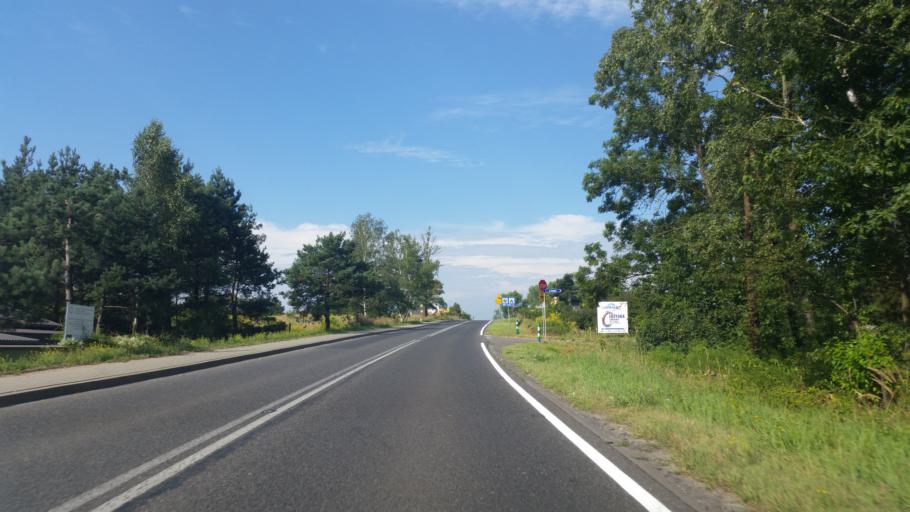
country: PL
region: Lesser Poland Voivodeship
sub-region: Powiat chrzanowski
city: Libiaz
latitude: 50.1116
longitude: 19.3439
